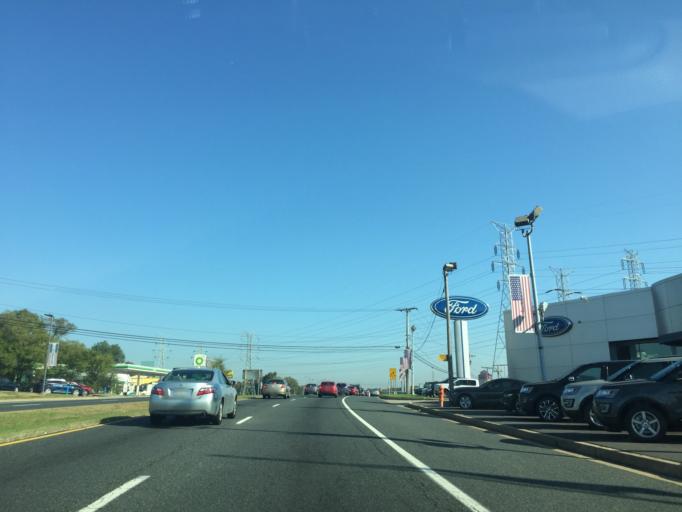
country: US
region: Maryland
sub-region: Baltimore County
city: Rosedale
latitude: 39.2858
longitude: -76.5063
